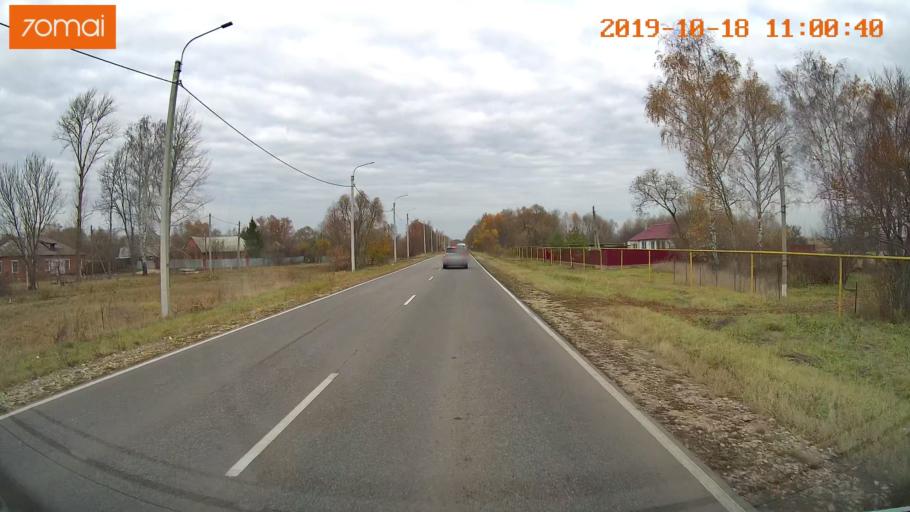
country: RU
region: Tula
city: Yepifan'
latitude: 53.8460
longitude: 38.5527
